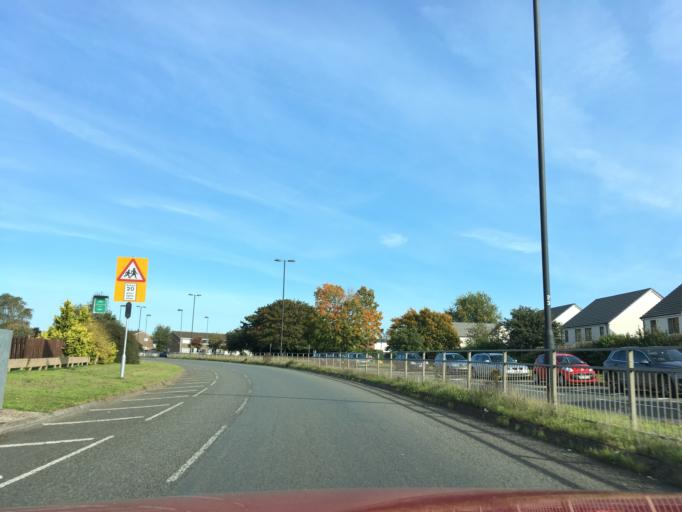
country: GB
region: England
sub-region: South Gloucestershire
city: Yate
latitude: 51.5284
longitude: -2.4251
